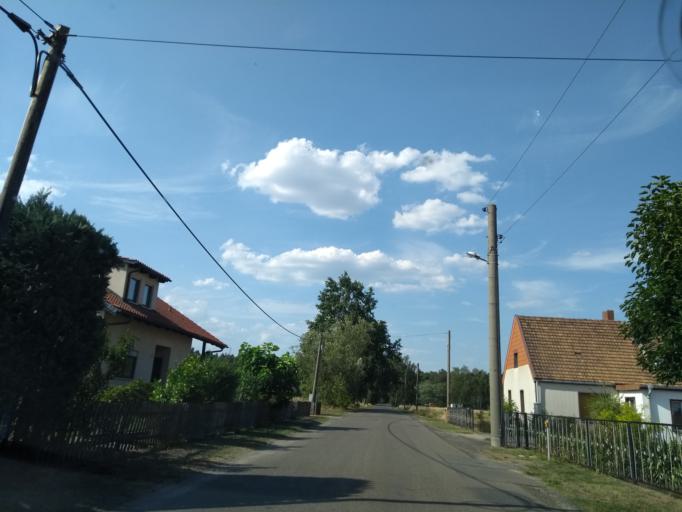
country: DE
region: Brandenburg
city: Luebben
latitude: 51.8556
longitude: 13.8500
